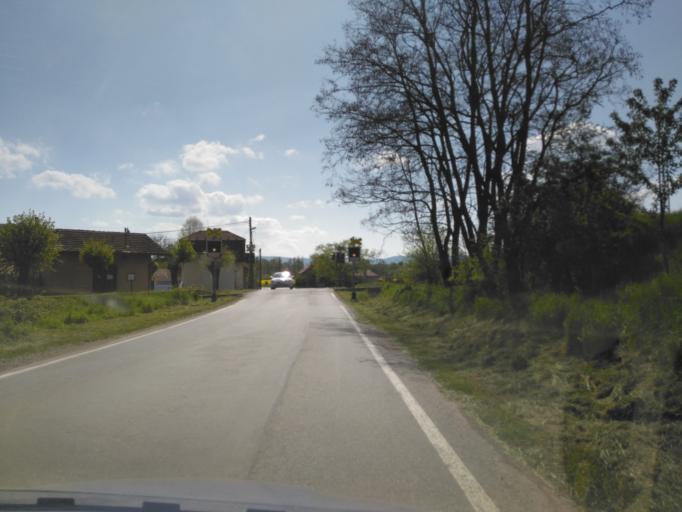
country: CZ
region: Central Bohemia
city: Lochovice
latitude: 49.8755
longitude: 13.9916
